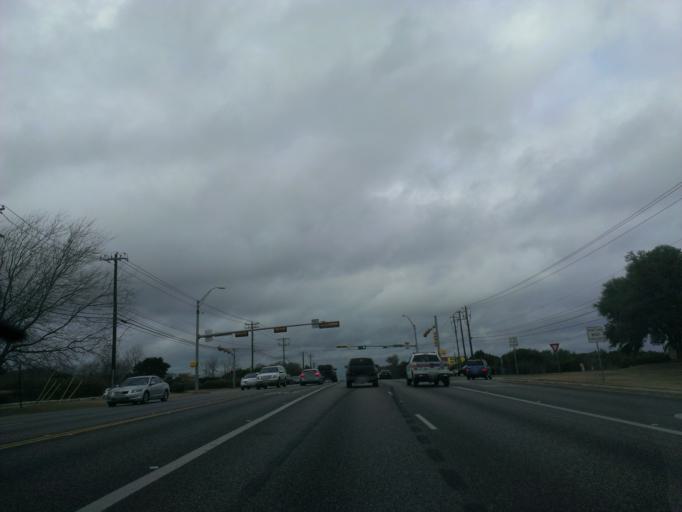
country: US
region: Texas
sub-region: Williamson County
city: Anderson Mill
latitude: 30.3940
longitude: -97.8448
